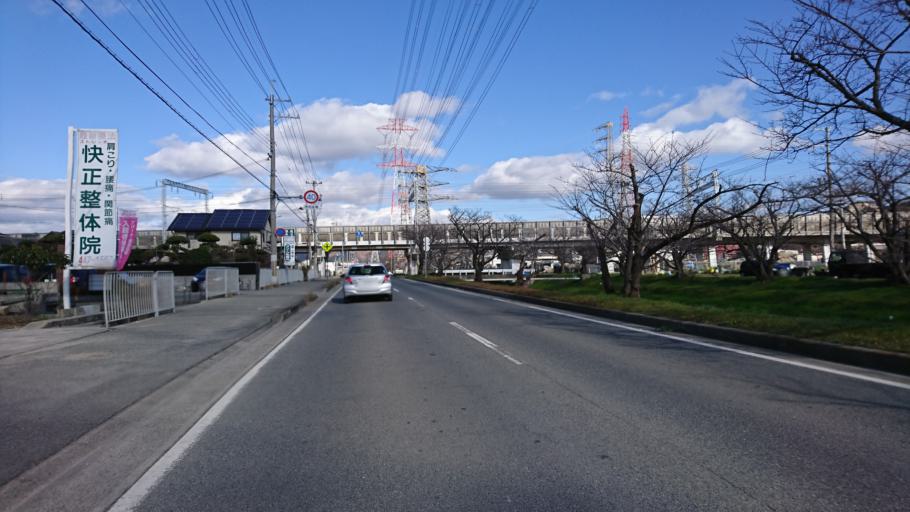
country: JP
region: Hyogo
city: Kakogawacho-honmachi
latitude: 34.7797
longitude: 134.7802
